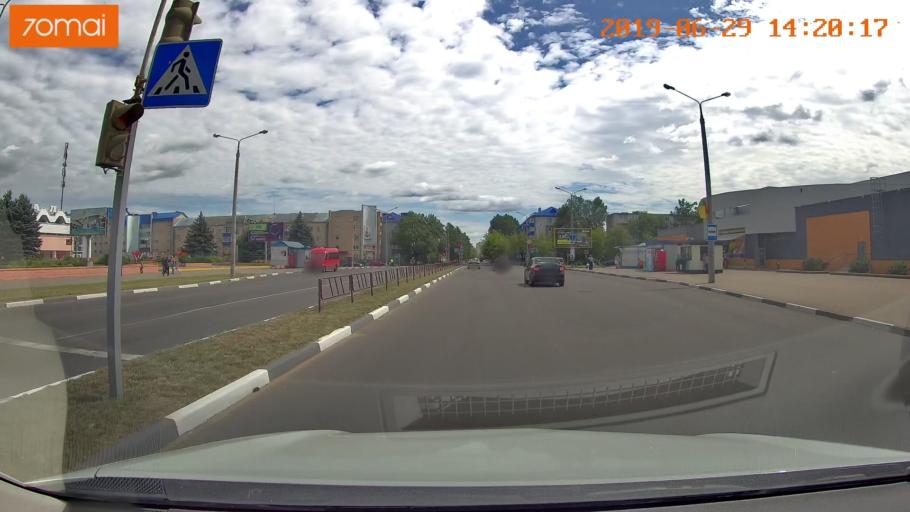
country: BY
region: Minsk
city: Salihorsk
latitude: 52.7931
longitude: 27.5426
